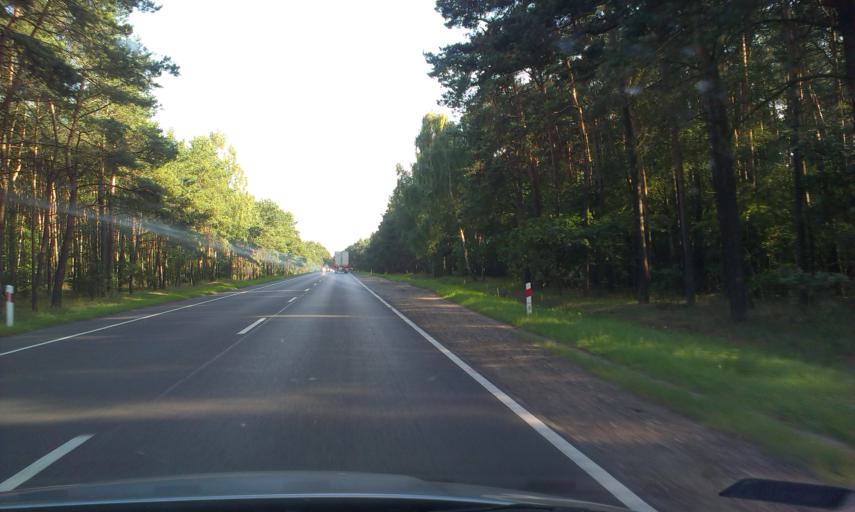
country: PL
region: Kujawsko-Pomorskie
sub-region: Powiat bydgoski
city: Biale Blota
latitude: 53.1163
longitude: 17.8831
